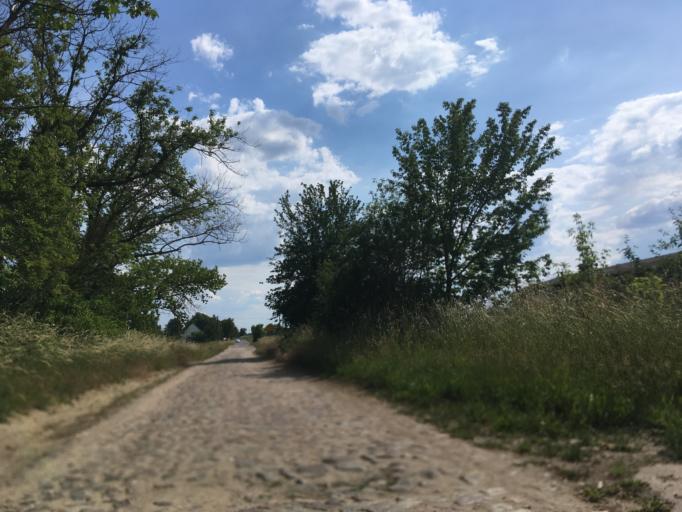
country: DE
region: Brandenburg
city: Muncheberg
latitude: 52.4511
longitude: 14.0957
